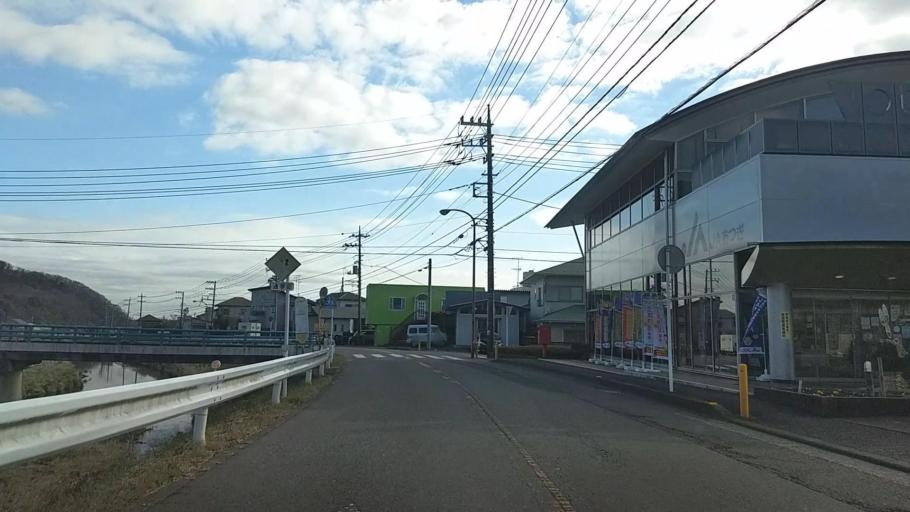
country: JP
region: Kanagawa
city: Isehara
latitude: 35.4354
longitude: 139.3076
